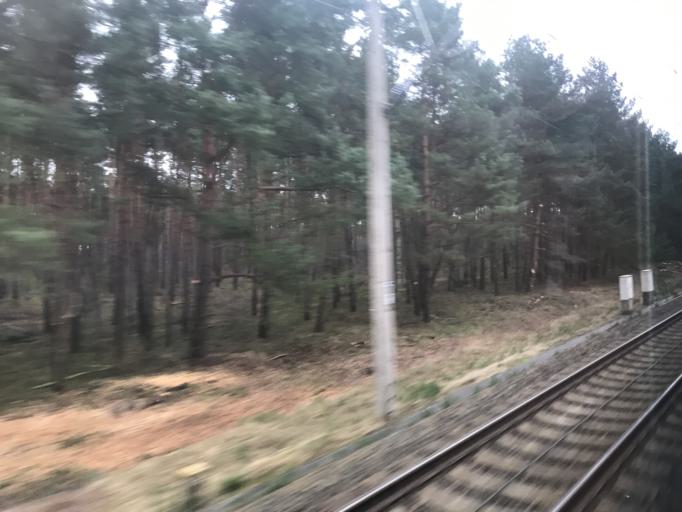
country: DE
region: Lower Saxony
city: Meinersen
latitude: 52.4562
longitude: 10.3695
